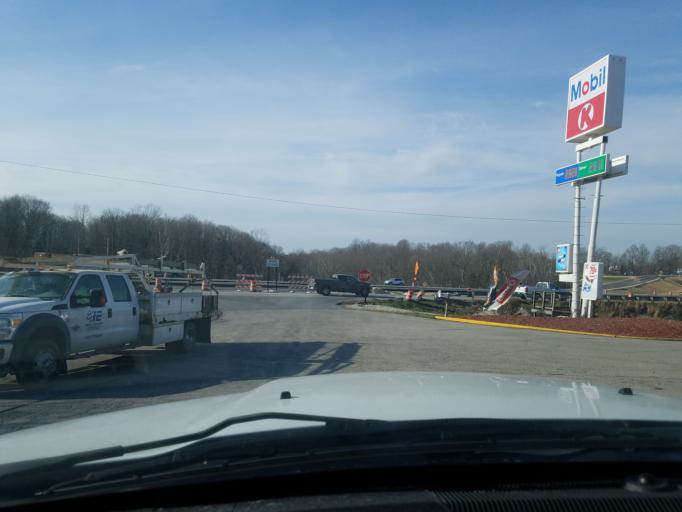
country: US
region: Indiana
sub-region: Monroe County
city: Bloomington
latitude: 39.2630
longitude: -86.5221
